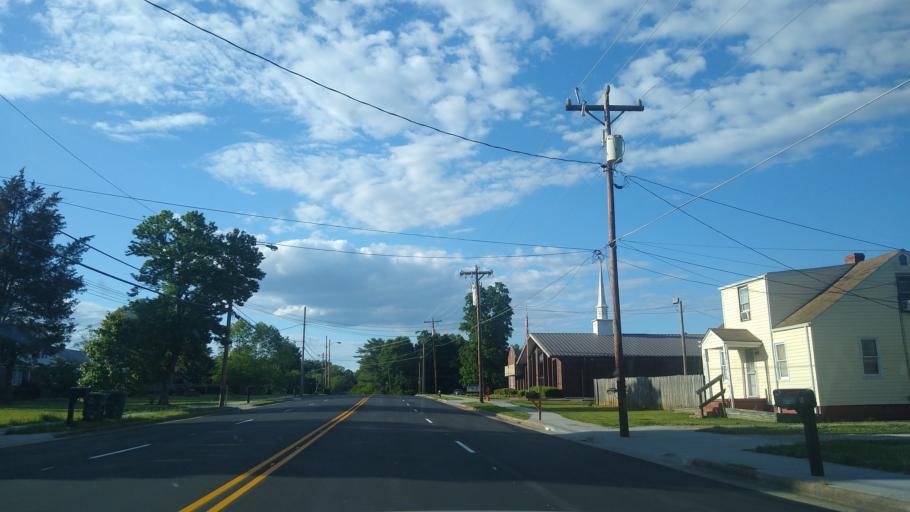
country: US
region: North Carolina
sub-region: Guilford County
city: Greensboro
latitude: 36.1299
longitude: -79.7747
